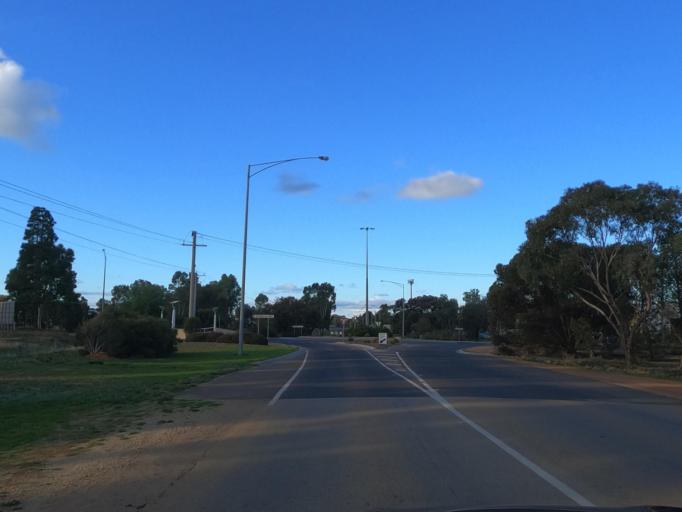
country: AU
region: Victoria
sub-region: Swan Hill
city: Swan Hill
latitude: -35.3433
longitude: 143.5306
